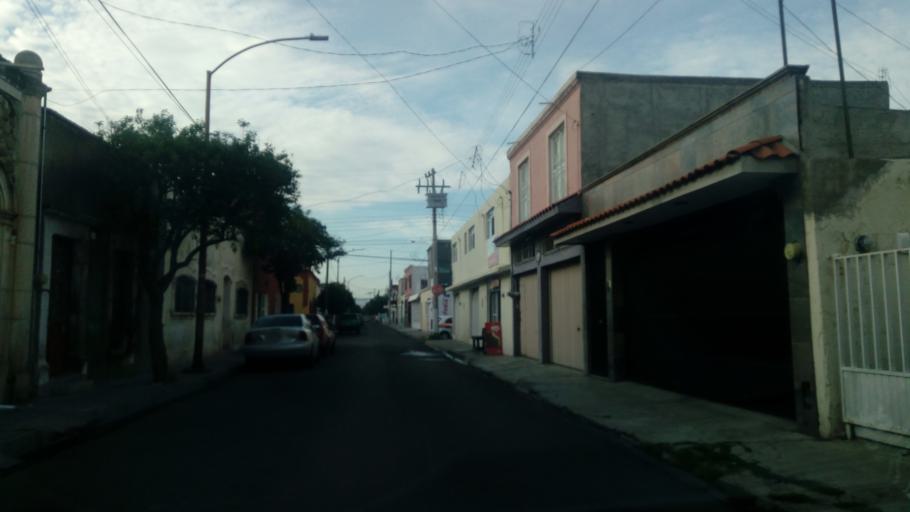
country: MX
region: Durango
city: Victoria de Durango
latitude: 24.0337
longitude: -104.6692
